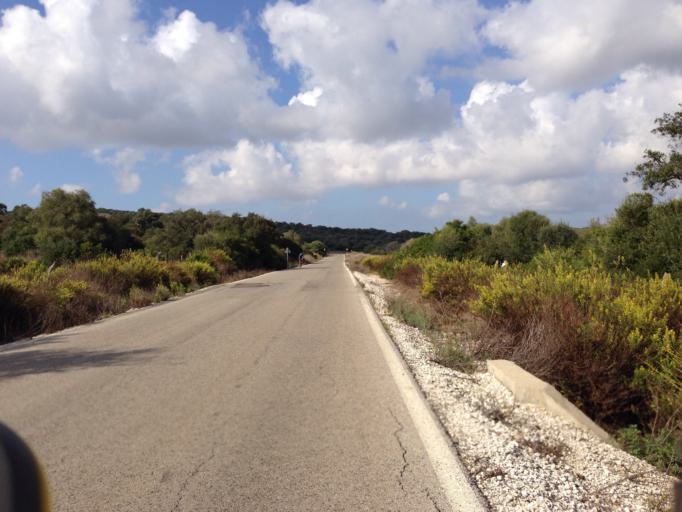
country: ES
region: Andalusia
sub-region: Provincia de Cadiz
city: Conil de la Frontera
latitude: 36.3428
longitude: -6.0138
